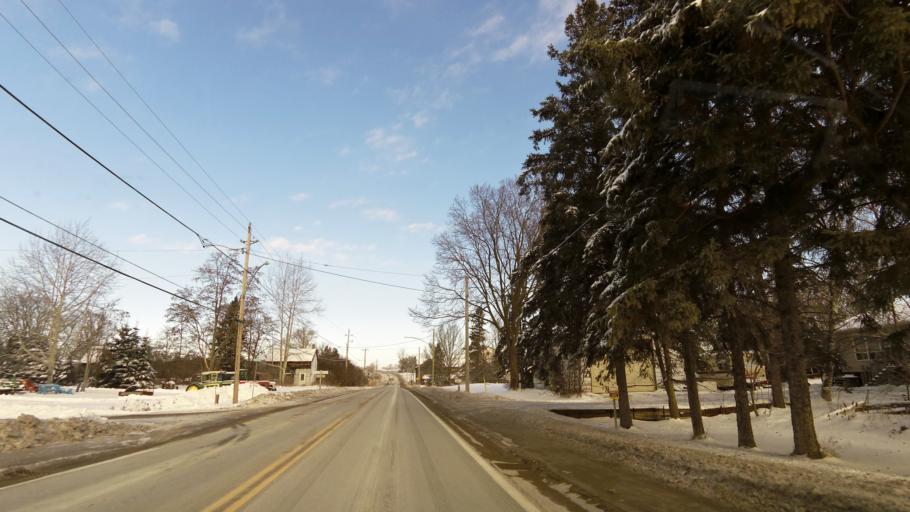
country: CA
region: Ontario
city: Quinte West
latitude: 44.1325
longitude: -77.7863
